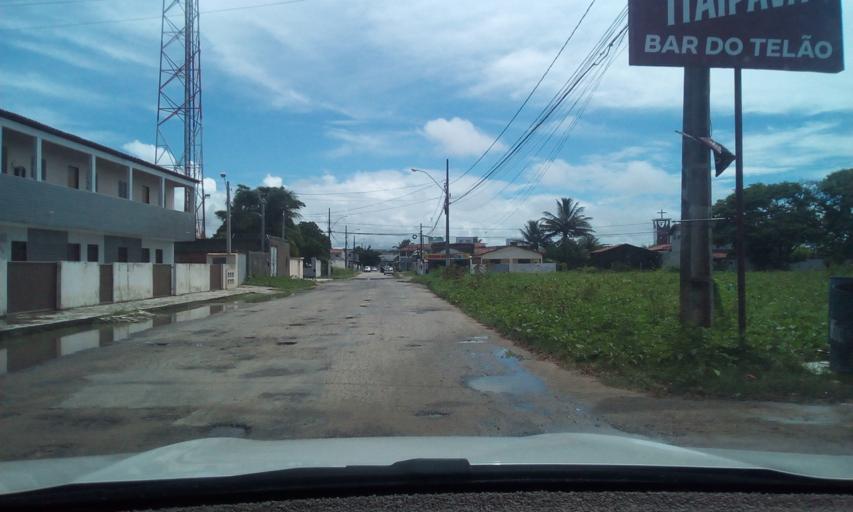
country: BR
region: Paraiba
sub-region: Cabedelo
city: Cabedelo
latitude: -7.0055
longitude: -34.8307
